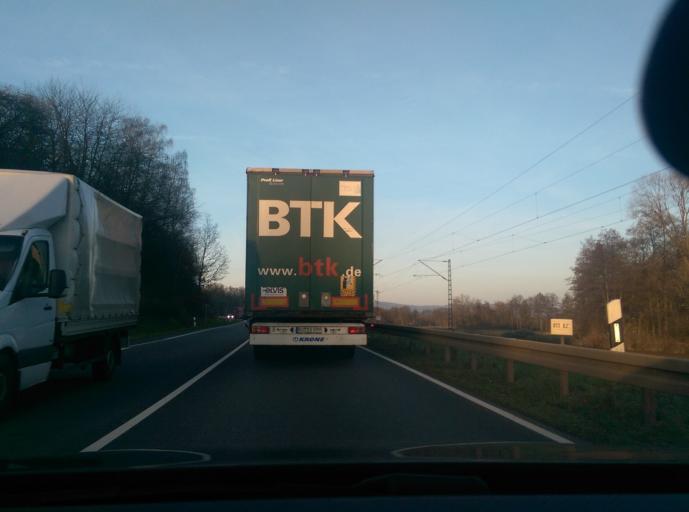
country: DE
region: Hesse
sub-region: Regierungsbezirk Kassel
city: Sontra
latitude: 51.1429
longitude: 9.9778
